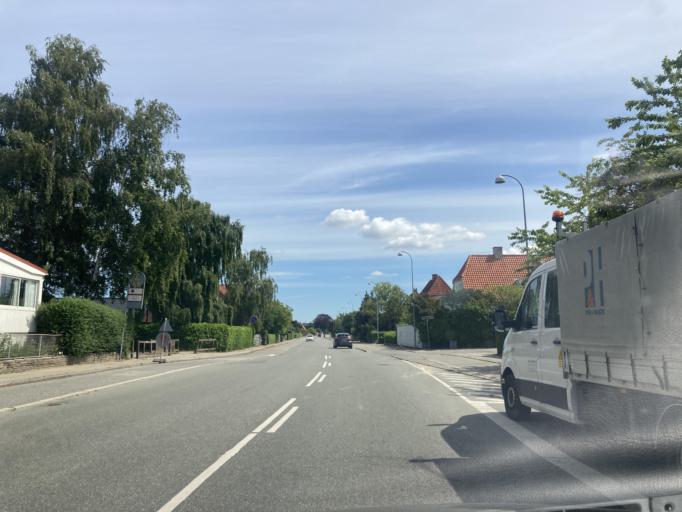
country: DK
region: Capital Region
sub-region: Hvidovre Kommune
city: Hvidovre
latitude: 55.6378
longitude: 12.4807
